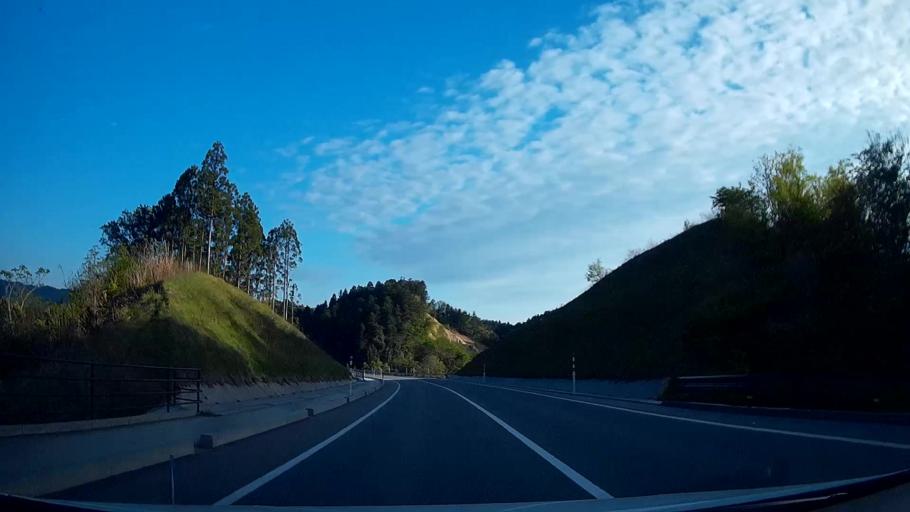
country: JP
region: Ishikawa
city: Nanao
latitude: 37.0377
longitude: 136.9475
